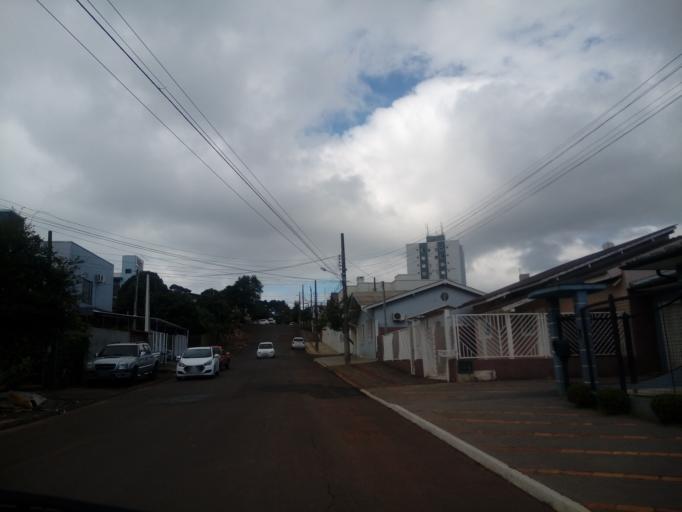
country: BR
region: Santa Catarina
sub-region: Chapeco
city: Chapeco
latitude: -27.1160
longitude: -52.6197
